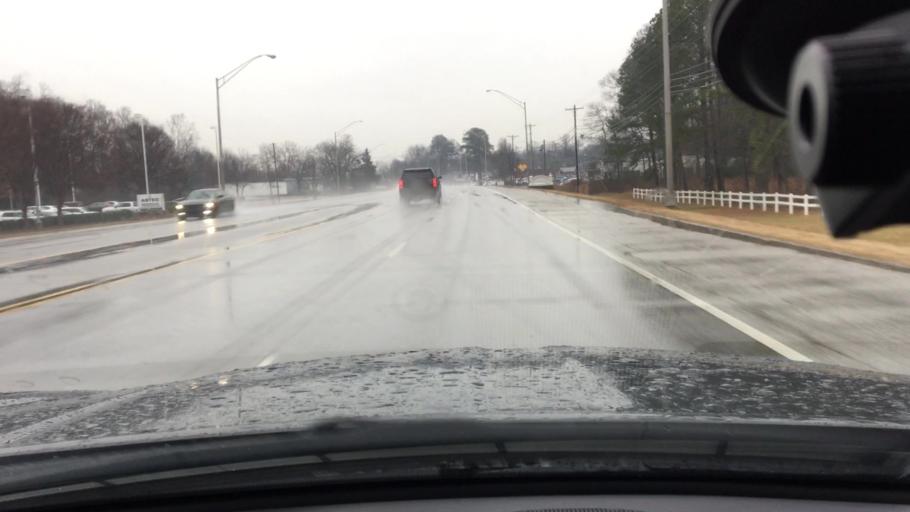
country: US
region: Tennessee
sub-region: Hamilton County
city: East Brainerd
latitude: 35.0378
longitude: -85.1903
